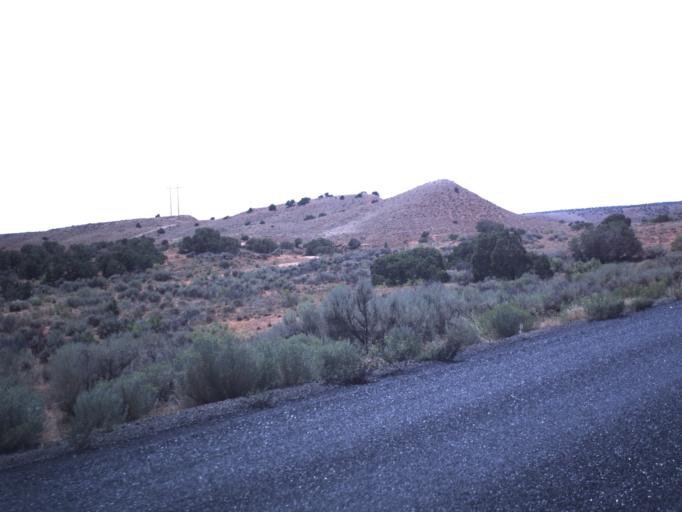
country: US
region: Utah
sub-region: Uintah County
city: Maeser
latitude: 40.4144
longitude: -109.6863
